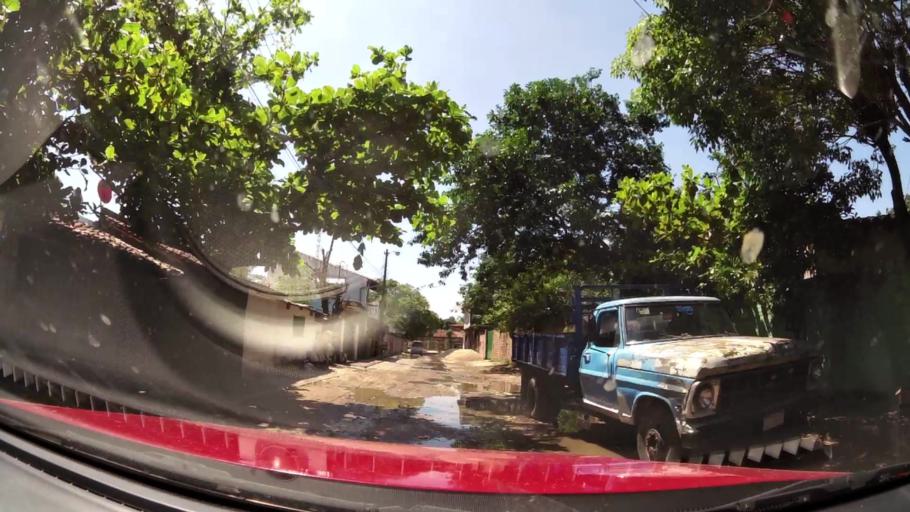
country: PY
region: Central
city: Colonia Mariano Roque Alonso
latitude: -25.2461
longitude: -57.5510
